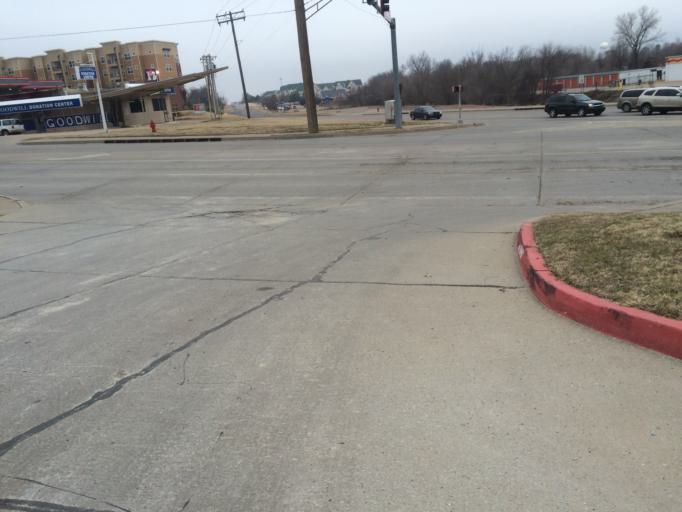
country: US
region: Oklahoma
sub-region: Cleveland County
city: Norman
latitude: 35.2041
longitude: -97.4310
